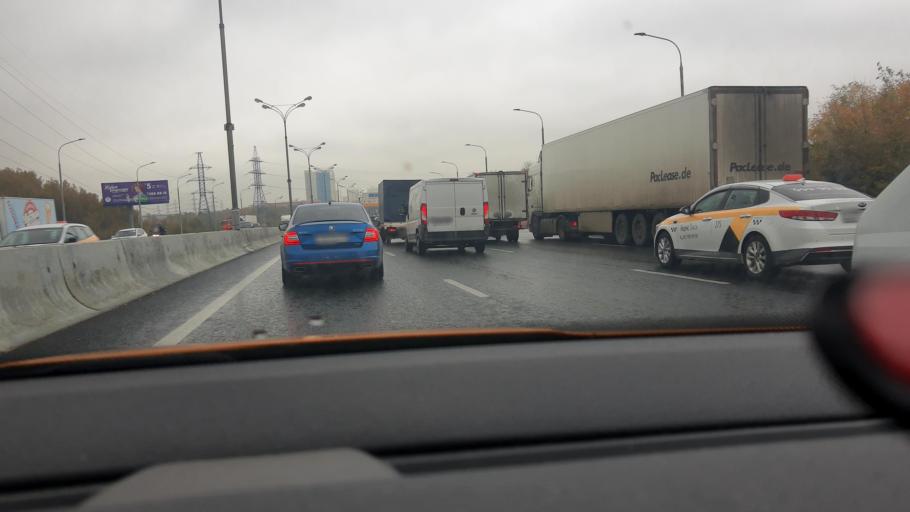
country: RU
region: Moscow
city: Vagonoremont
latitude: 55.9030
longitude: 37.5249
